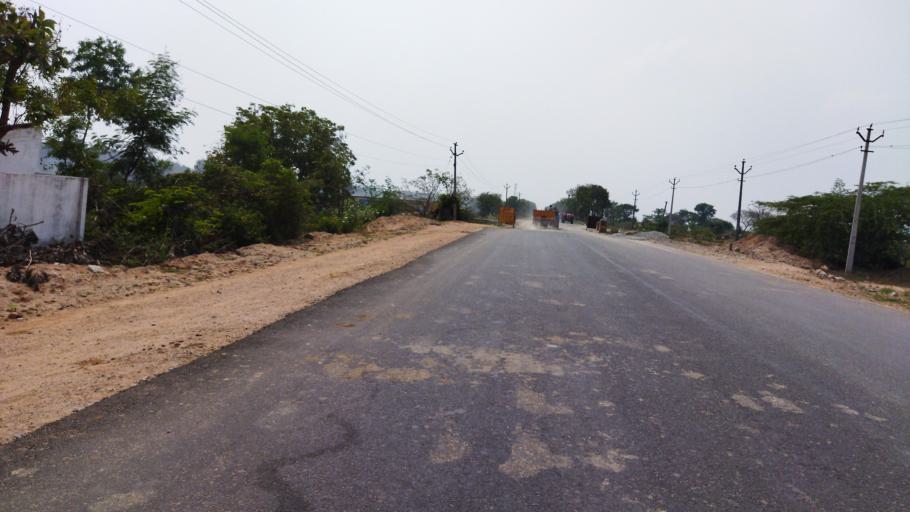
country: IN
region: Telangana
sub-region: Nalgonda
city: Nalgonda
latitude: 17.0848
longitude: 79.3247
